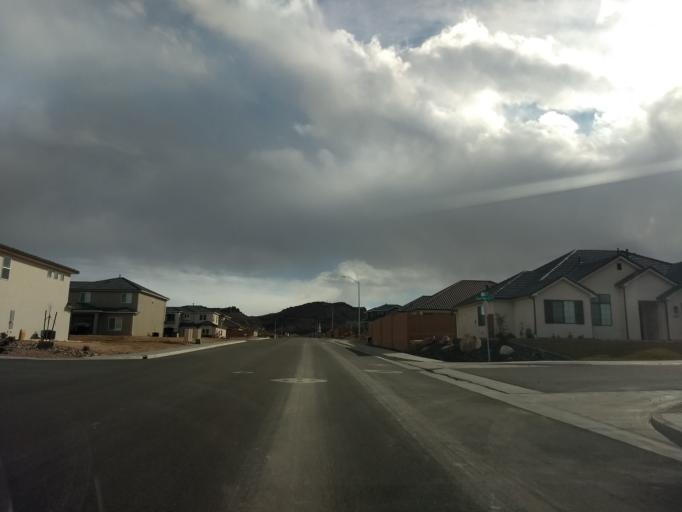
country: US
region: Utah
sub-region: Washington County
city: Washington
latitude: 37.0572
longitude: -113.5176
